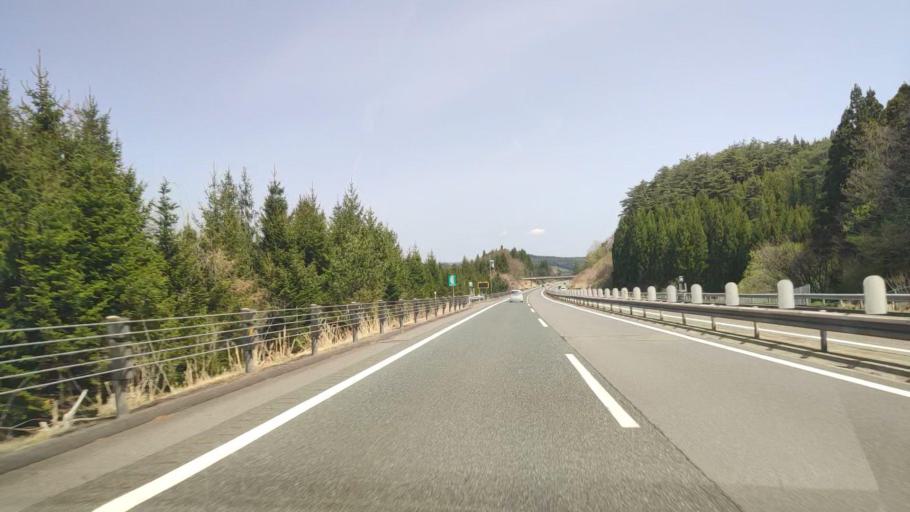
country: JP
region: Iwate
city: Ichinohe
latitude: 40.1482
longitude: 141.1172
